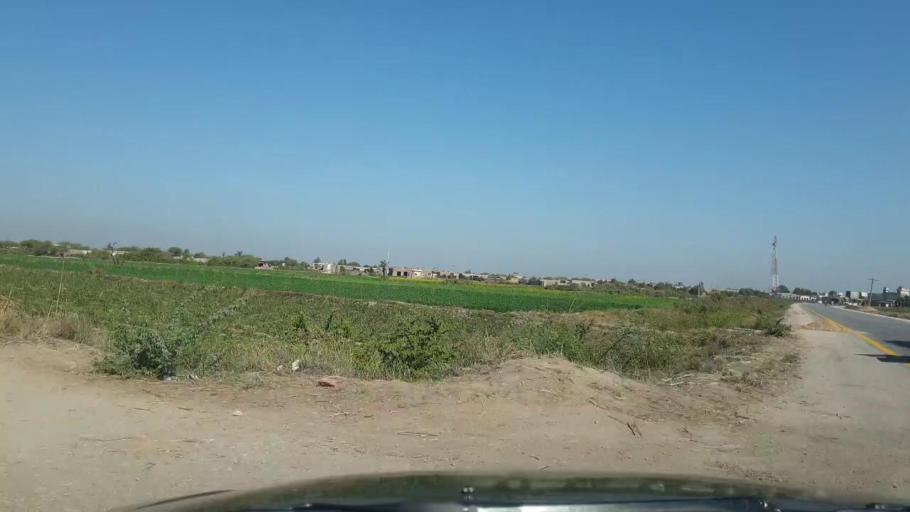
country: PK
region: Sindh
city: Mirpur Khas
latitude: 25.5673
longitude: 69.0629
